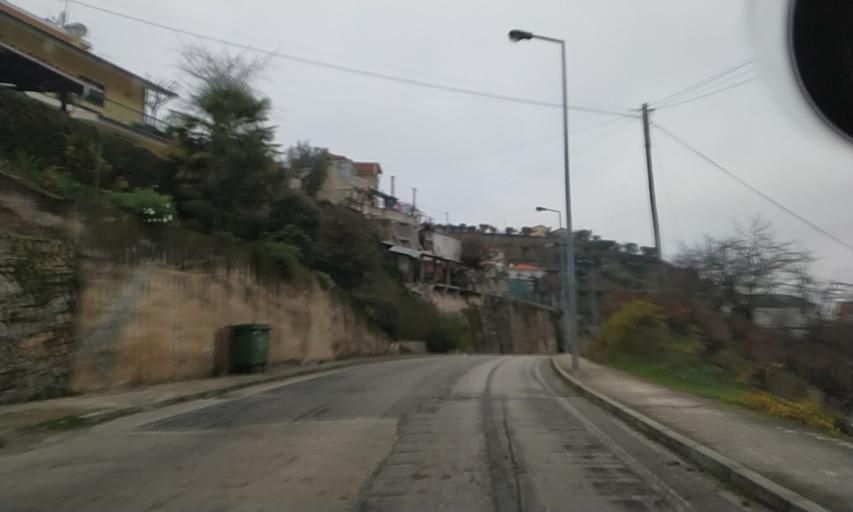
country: PT
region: Viseu
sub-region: Lamego
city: Lamego
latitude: 41.1254
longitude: -7.8043
